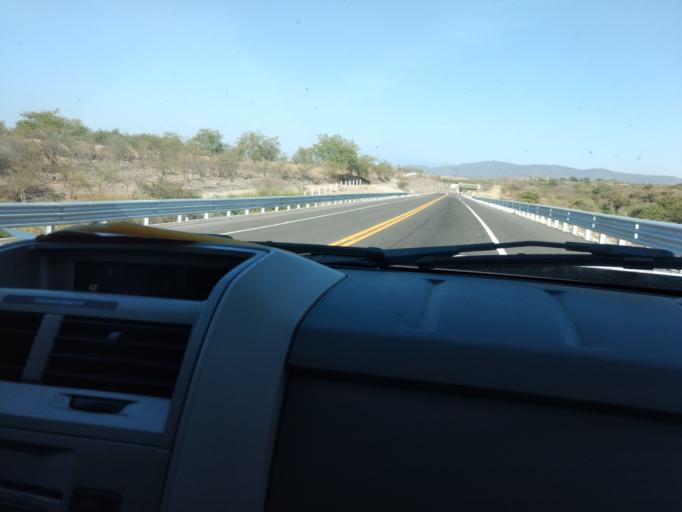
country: MX
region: Morelos
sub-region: Ayala
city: El Salitre
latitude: 18.6701
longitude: -98.9577
